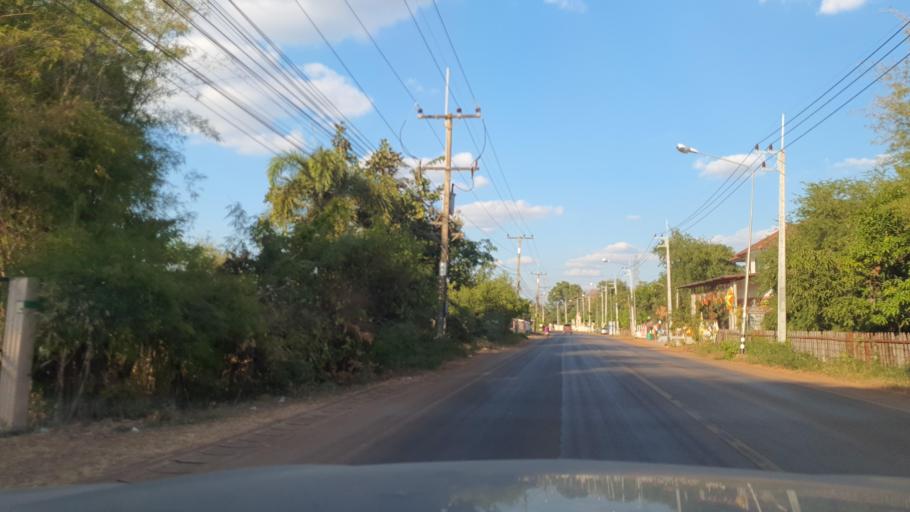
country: TH
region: Sakon Nakhon
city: Phon Na Kaeo
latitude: 17.2619
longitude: 104.1905
